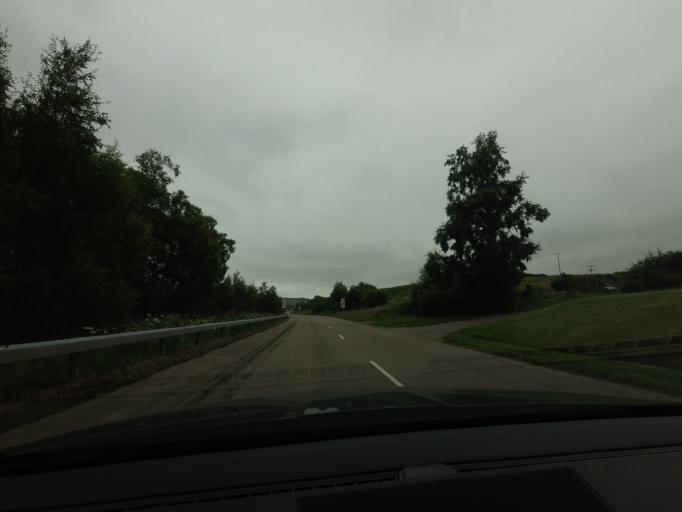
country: GB
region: Scotland
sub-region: Highland
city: Alness
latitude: 58.0163
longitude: -4.4023
